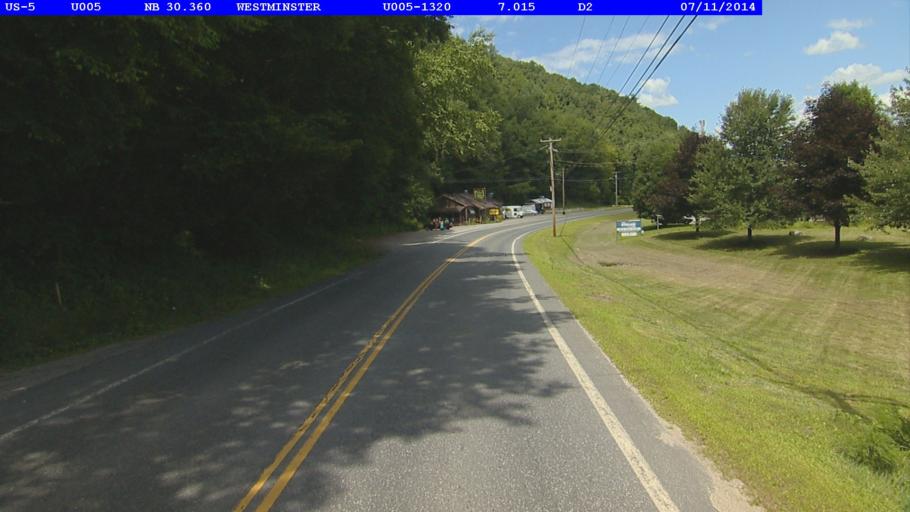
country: US
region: Vermont
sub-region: Windham County
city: Bellows Falls
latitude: 43.1103
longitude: -72.4418
